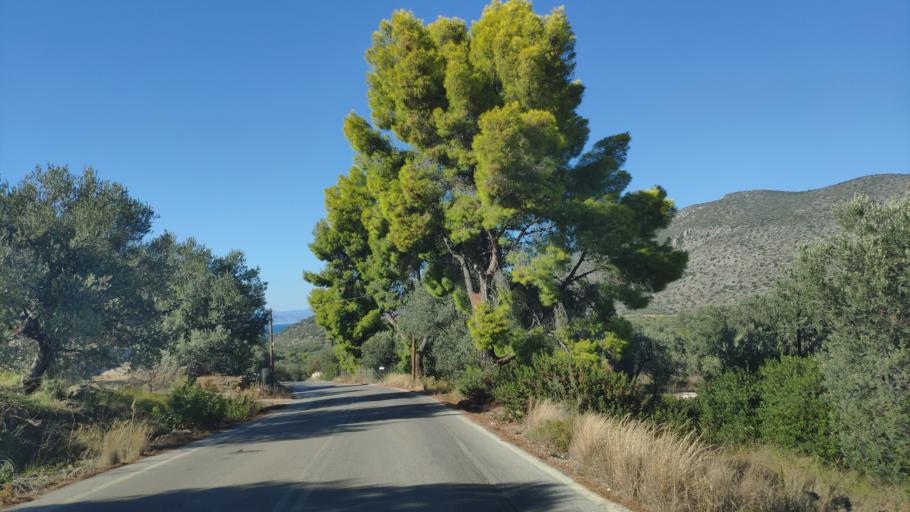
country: GR
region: Attica
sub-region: Nomos Piraios
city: Galatas
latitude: 37.5476
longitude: 23.3756
